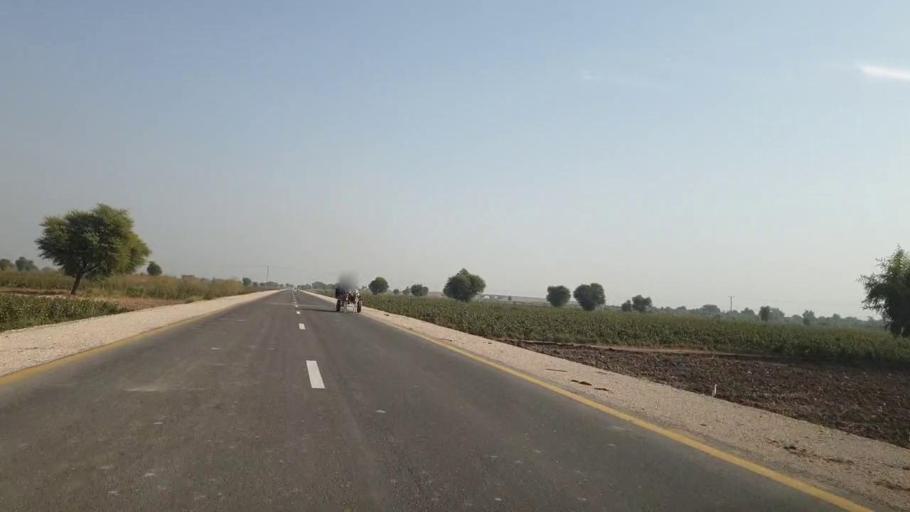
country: PK
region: Sindh
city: Sehwan
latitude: 26.4652
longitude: 67.7980
